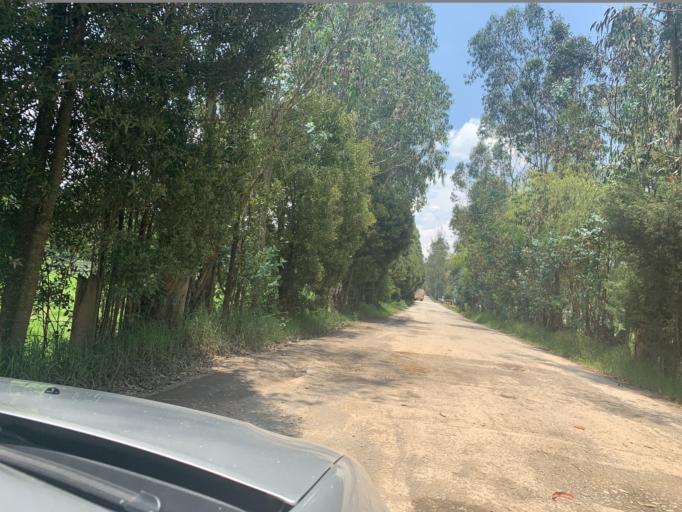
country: CO
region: Boyaca
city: Chiquinquira
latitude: 5.5682
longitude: -73.7490
